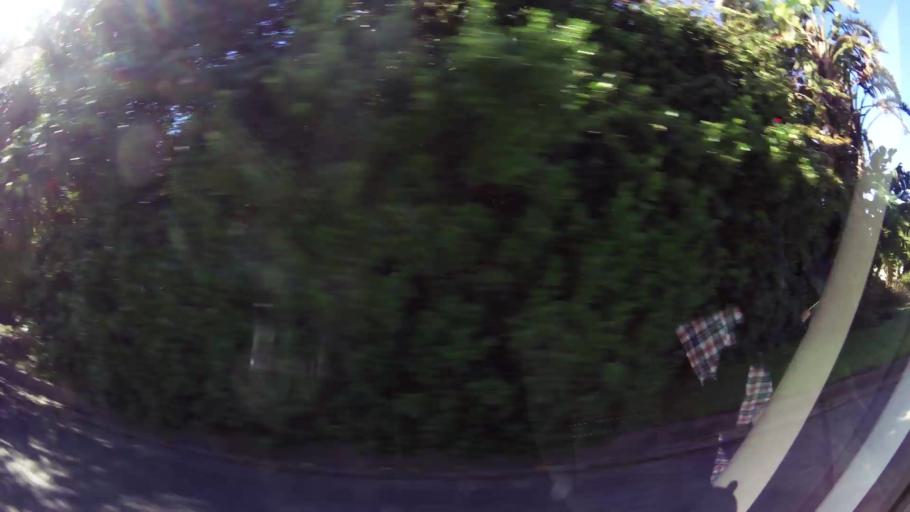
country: ZA
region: Western Cape
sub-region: Eden District Municipality
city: George
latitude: -33.9515
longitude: 22.4564
